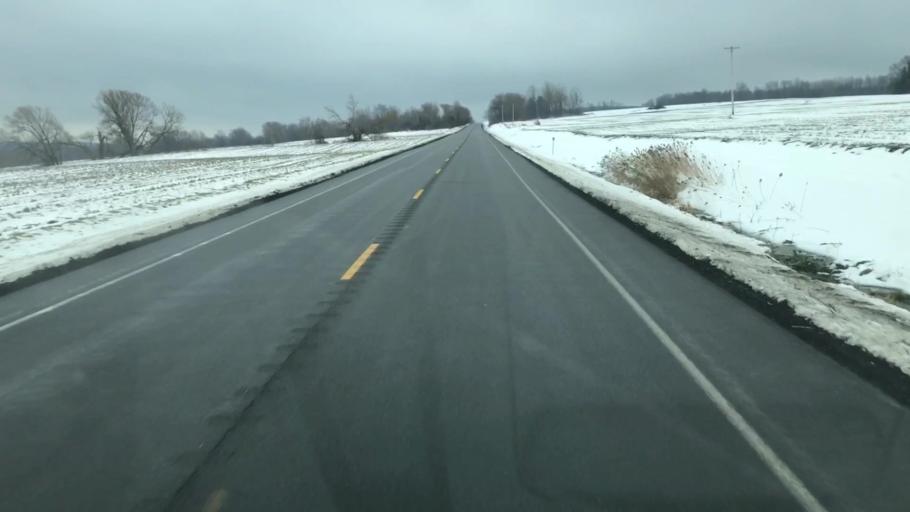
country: US
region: New York
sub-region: Cayuga County
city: Moravia
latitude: 42.7827
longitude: -76.3421
